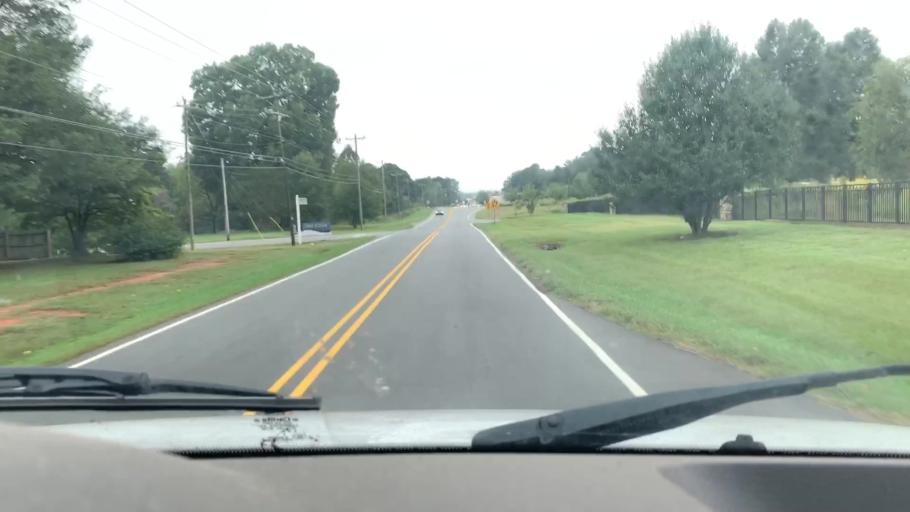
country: US
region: North Carolina
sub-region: Gaston County
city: Davidson
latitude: 35.5357
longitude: -80.8526
